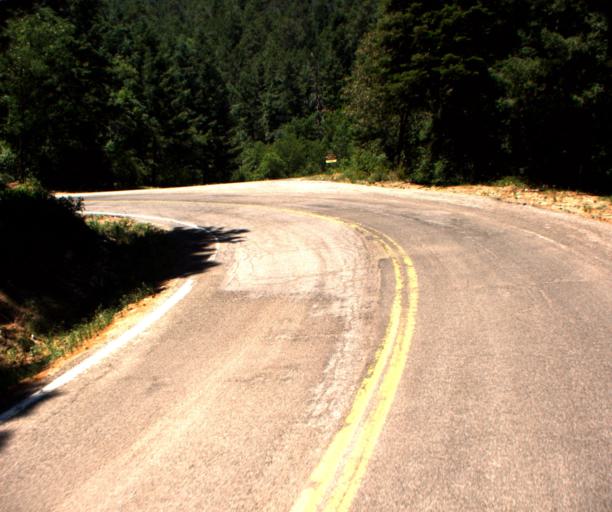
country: US
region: Arizona
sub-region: Graham County
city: Swift Trail Junction
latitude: 32.6297
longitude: -109.8210
